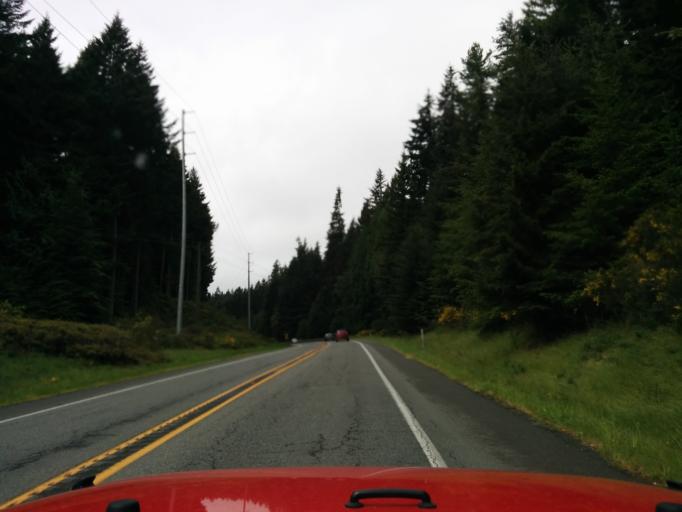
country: US
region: Washington
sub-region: Island County
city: Langley
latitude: 48.0042
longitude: -122.4368
